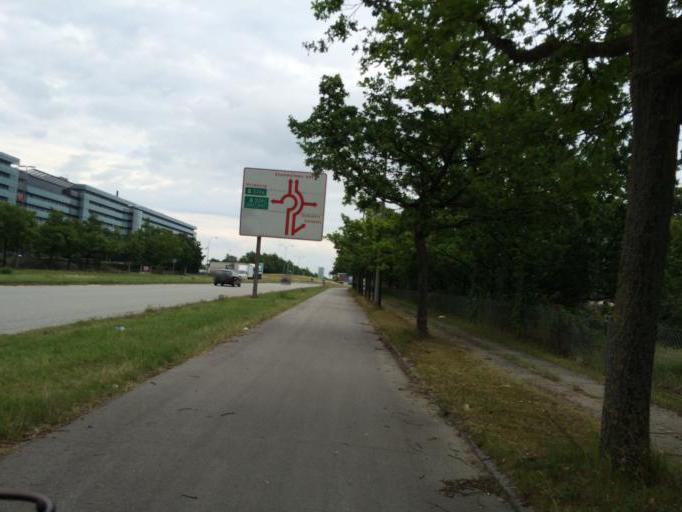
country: DK
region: Capital Region
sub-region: Hvidovre Kommune
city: Hvidovre
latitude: 55.6142
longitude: 12.4727
